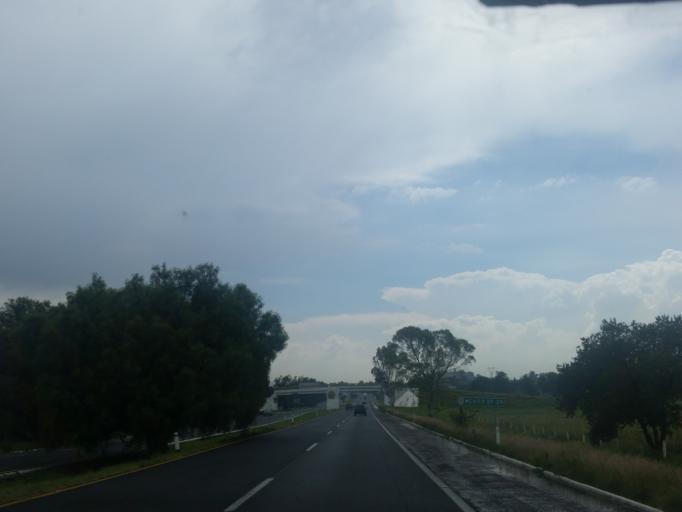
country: MX
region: Mexico
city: Acolman
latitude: 19.6288
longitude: -98.9186
